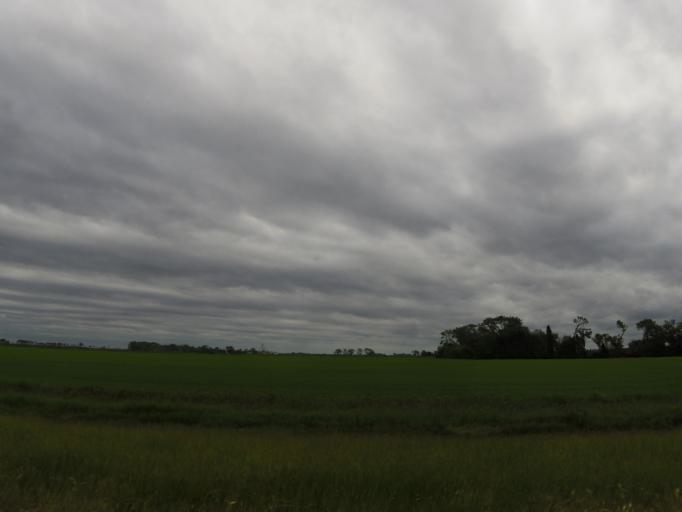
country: US
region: North Dakota
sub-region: Walsh County
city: Grafton
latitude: 48.5166
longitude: -97.4477
